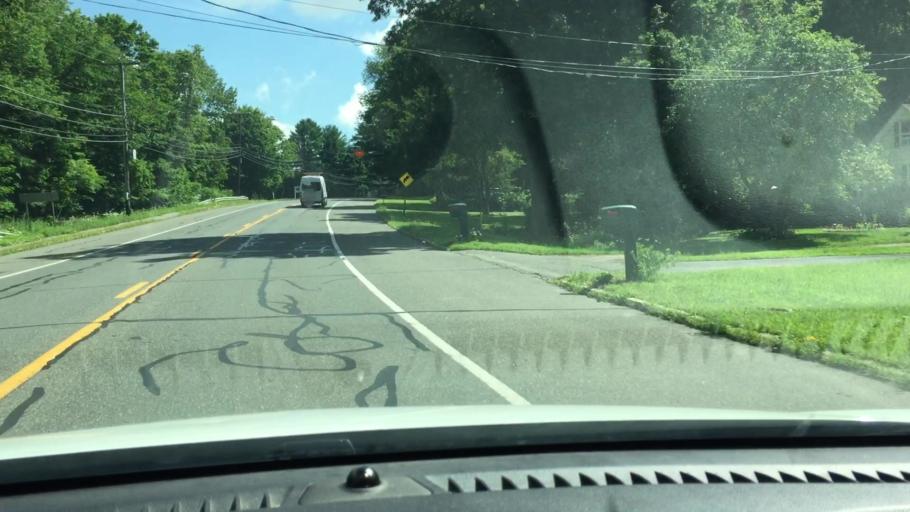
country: US
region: Massachusetts
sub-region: Berkshire County
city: Pittsfield
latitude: 42.4387
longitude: -73.3016
